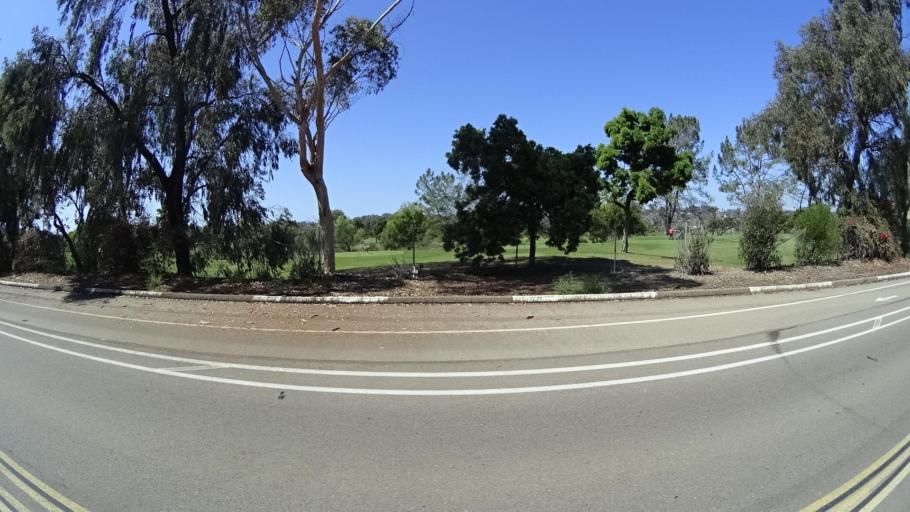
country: US
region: California
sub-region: San Diego County
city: Fairbanks Ranch
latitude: 32.9828
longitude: -117.2054
